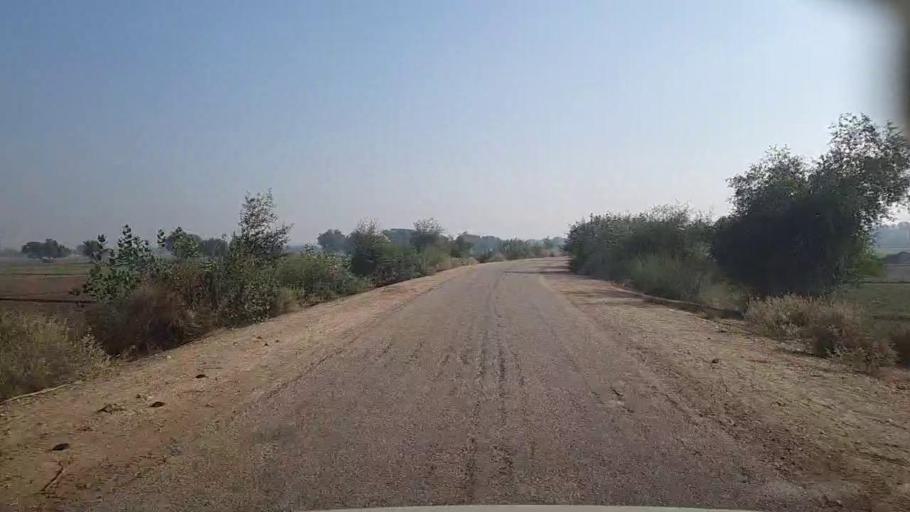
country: PK
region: Sindh
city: Kandiari
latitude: 26.8189
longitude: 68.4947
